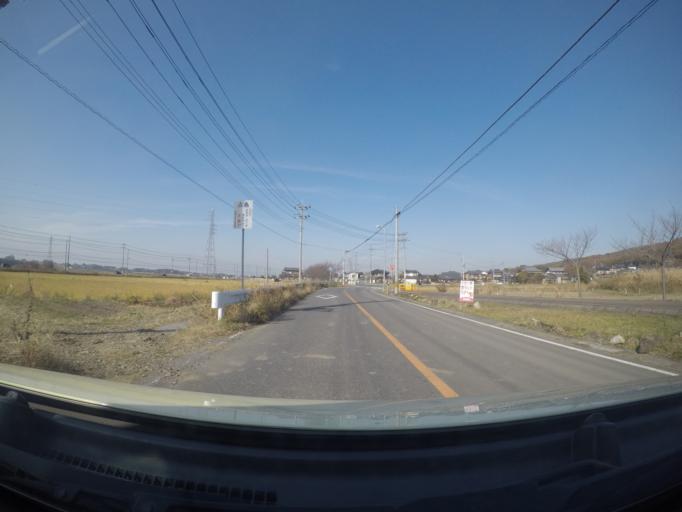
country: JP
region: Ibaraki
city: Tsukuba
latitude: 36.2175
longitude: 140.0677
